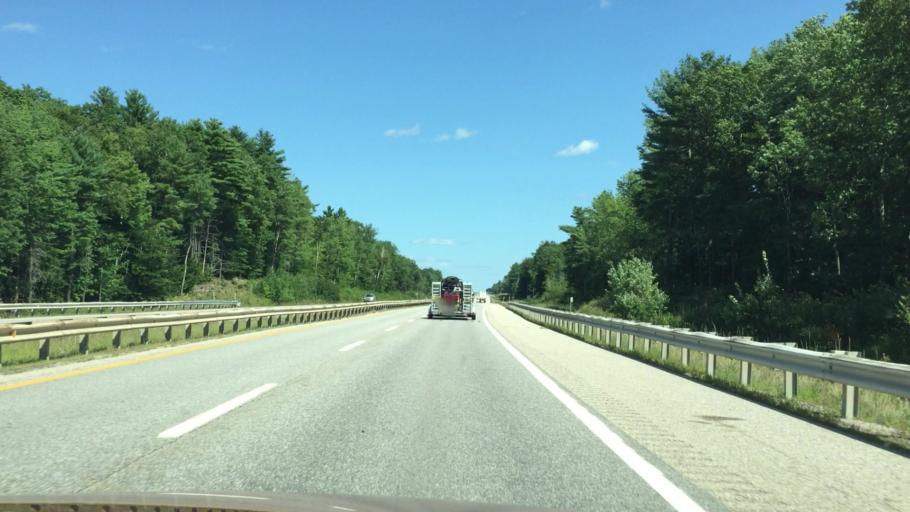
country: US
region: Maine
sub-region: Androscoggin County
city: Sabattus
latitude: 44.1242
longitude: -70.0334
